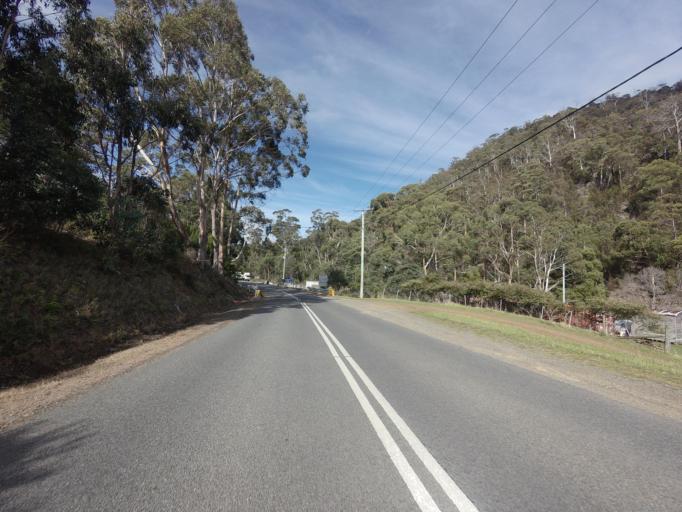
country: AU
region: Tasmania
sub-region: Clarence
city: Sandford
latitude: -43.1127
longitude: 147.7492
